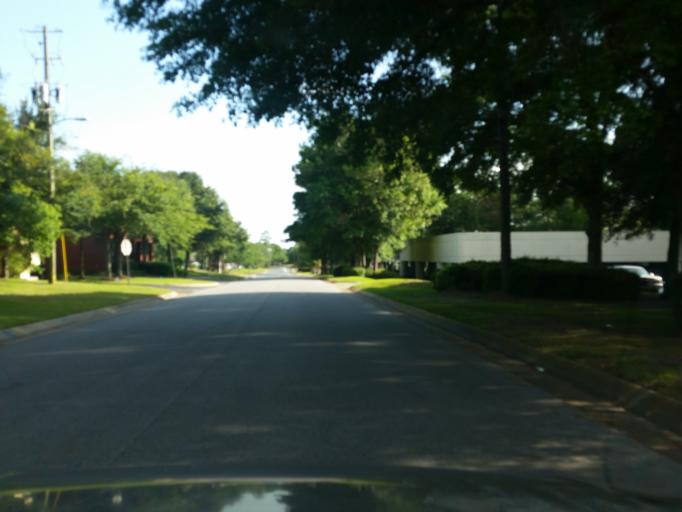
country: US
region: Florida
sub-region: Escambia County
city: Ferry Pass
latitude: 30.4766
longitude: -87.1998
